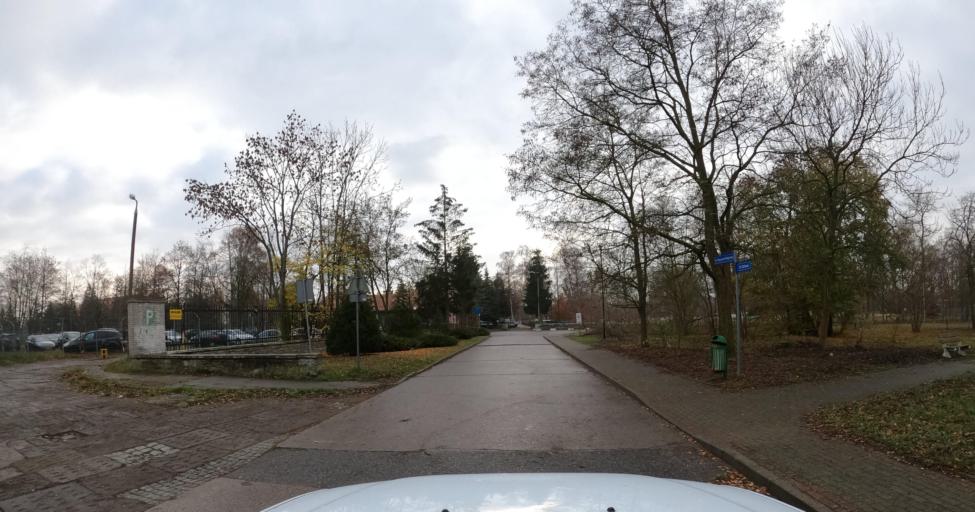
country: PL
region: West Pomeranian Voivodeship
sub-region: Powiat kamienski
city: Dziwnow
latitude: 54.0172
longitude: 14.7476
